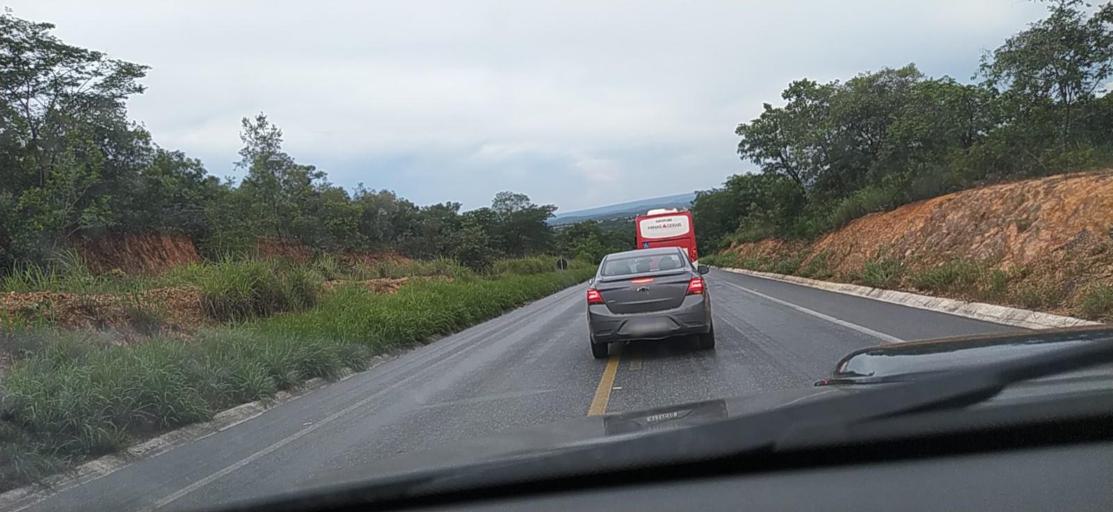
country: BR
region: Minas Gerais
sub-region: Montes Claros
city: Montes Claros
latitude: -16.6620
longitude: -43.7641
